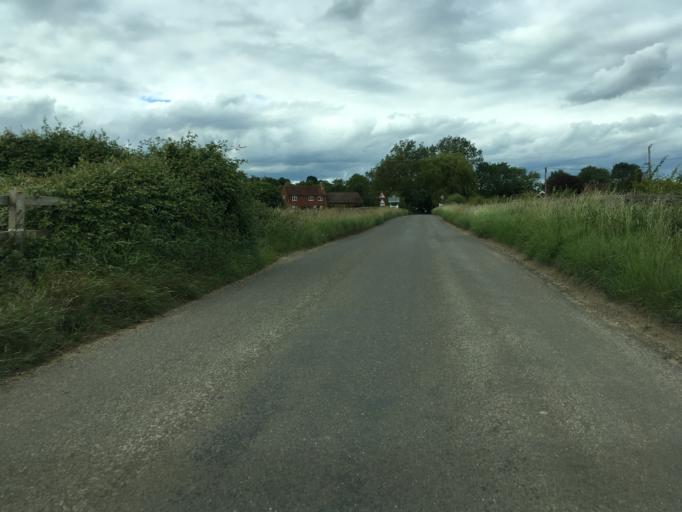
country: GB
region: England
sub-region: Oxfordshire
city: Boars Hill
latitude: 51.6987
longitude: -1.2892
